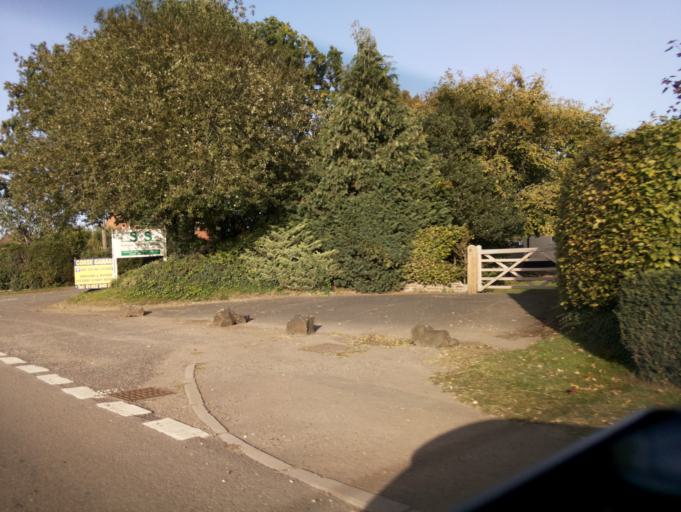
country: GB
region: England
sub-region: Gloucestershire
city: Newent
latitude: 51.9593
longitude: -2.3041
